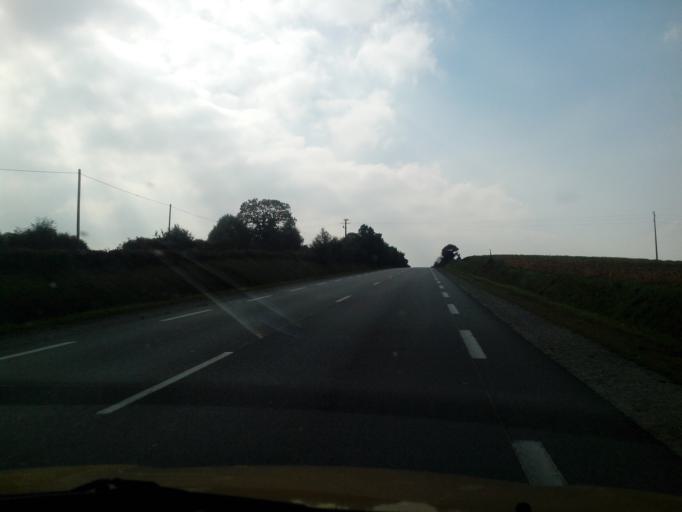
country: FR
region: Brittany
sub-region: Departement du Morbihan
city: Loyat
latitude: 47.9876
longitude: -2.3688
